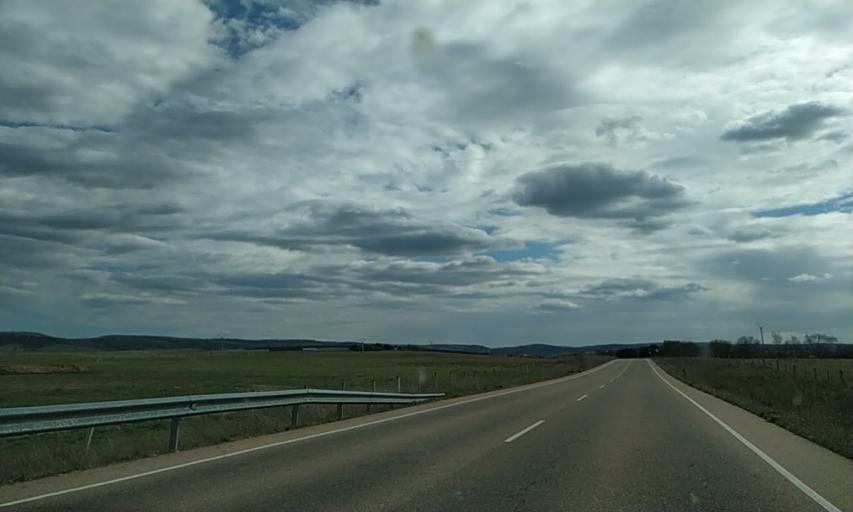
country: ES
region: Castille and Leon
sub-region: Provincia de Salamanca
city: Pastores
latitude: 40.5447
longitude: -6.5620
